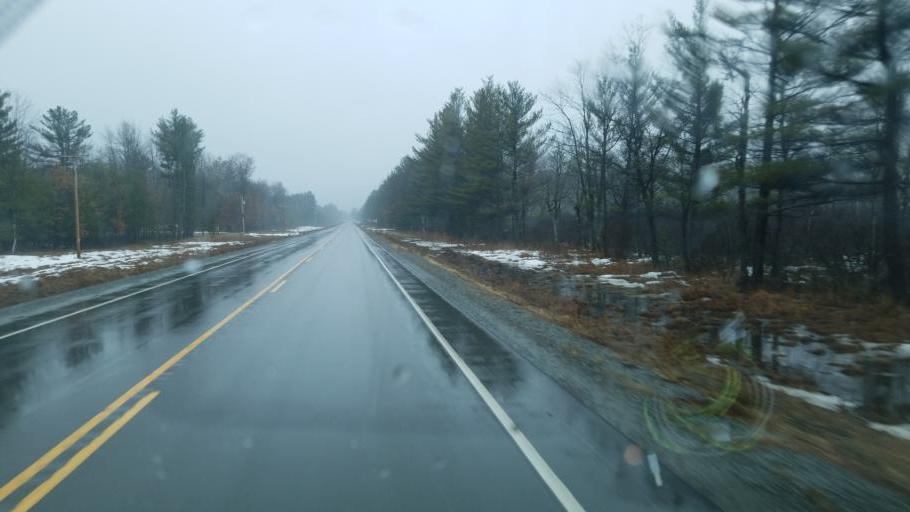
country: US
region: Wisconsin
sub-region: Clark County
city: Neillsville
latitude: 44.4878
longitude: -90.3558
